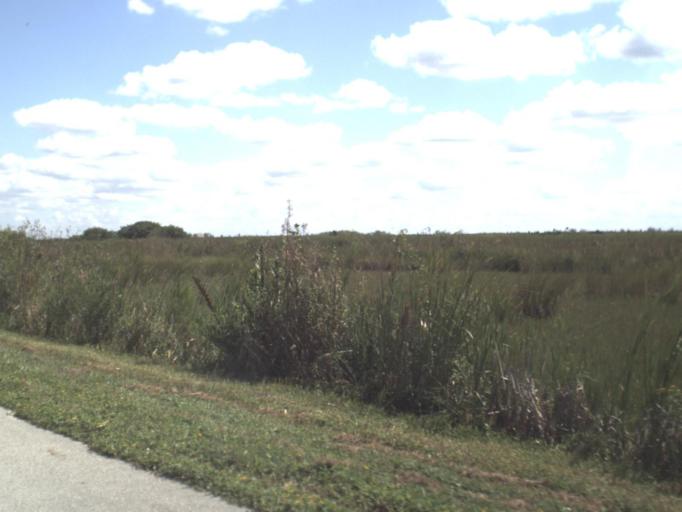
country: US
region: Florida
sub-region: Collier County
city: Marco
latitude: 25.9187
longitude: -81.3938
